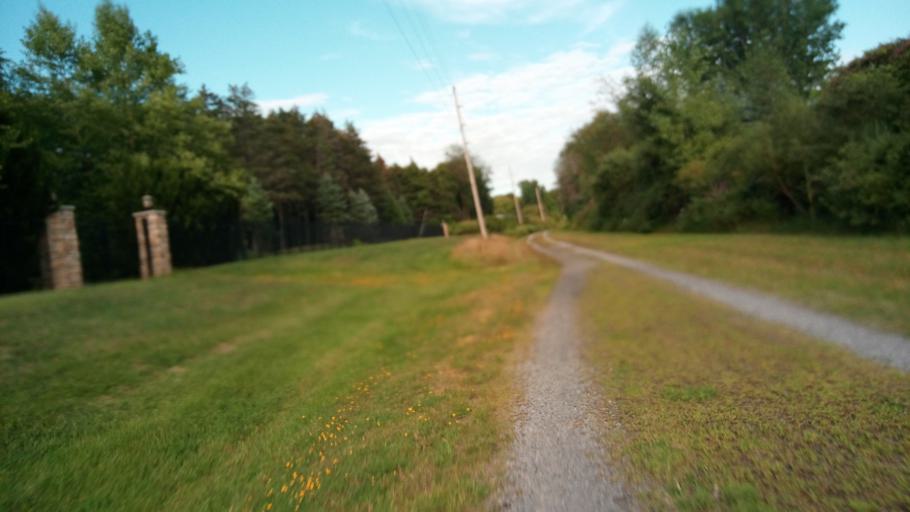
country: US
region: New York
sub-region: Ontario County
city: Victor
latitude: 43.0028
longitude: -77.4874
